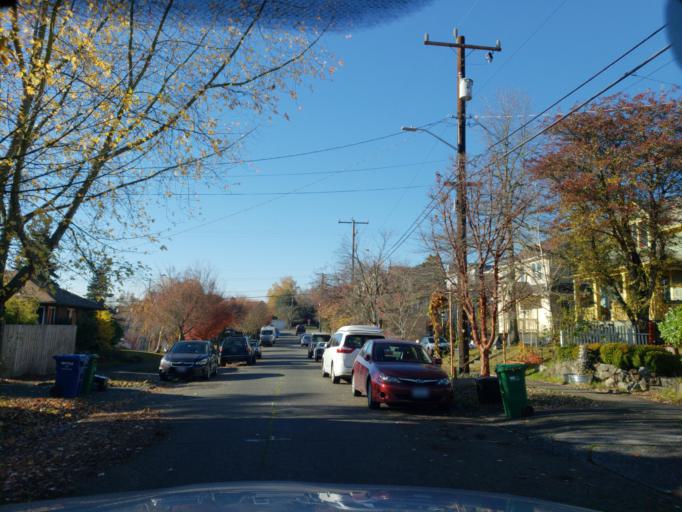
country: US
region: Washington
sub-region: King County
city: Seattle
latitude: 47.6742
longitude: -122.3643
